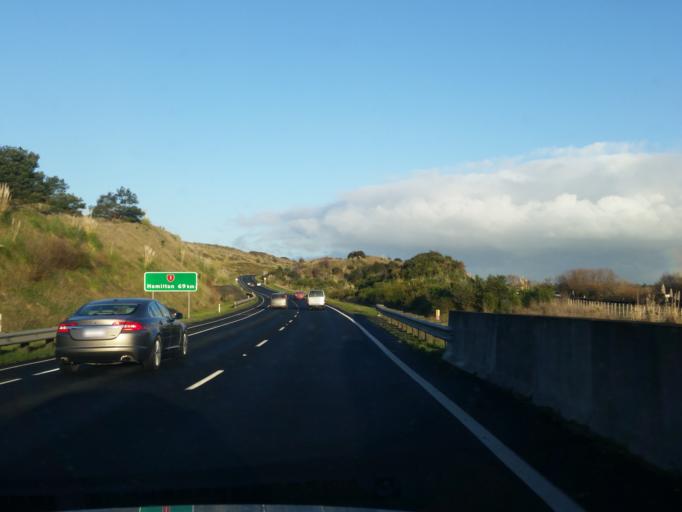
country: NZ
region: Auckland
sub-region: Auckland
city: Pukekohe East
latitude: -37.2850
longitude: 175.0524
